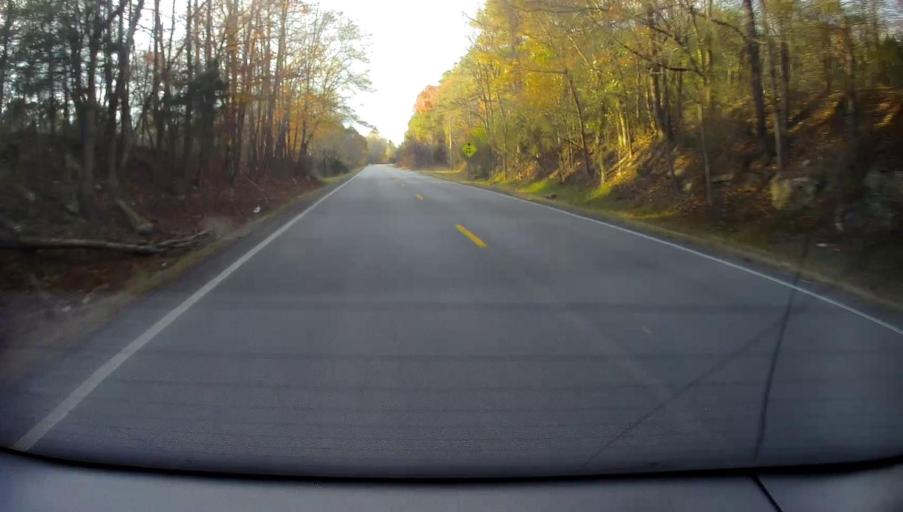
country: US
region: Alabama
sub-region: Blount County
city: Blountsville
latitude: 34.1782
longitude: -86.5150
